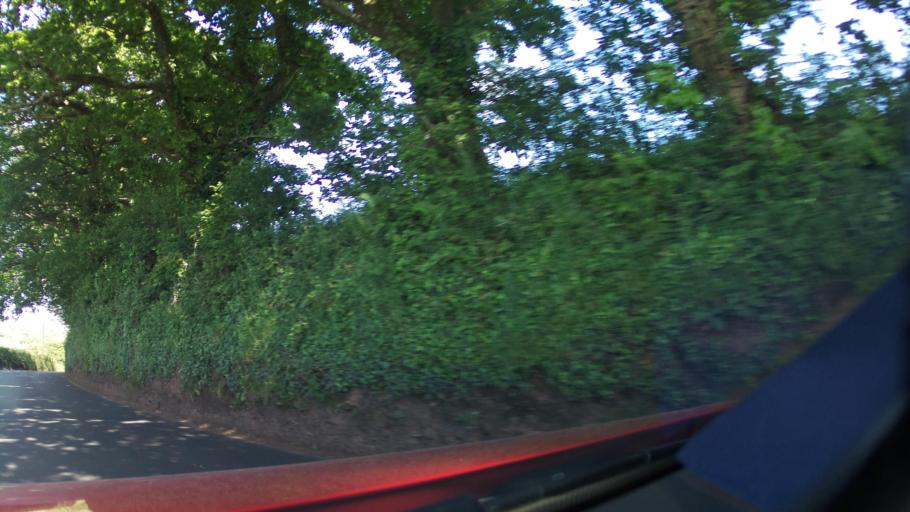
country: GB
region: England
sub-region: Devon
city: Marldon
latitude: 50.4491
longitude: -3.6081
